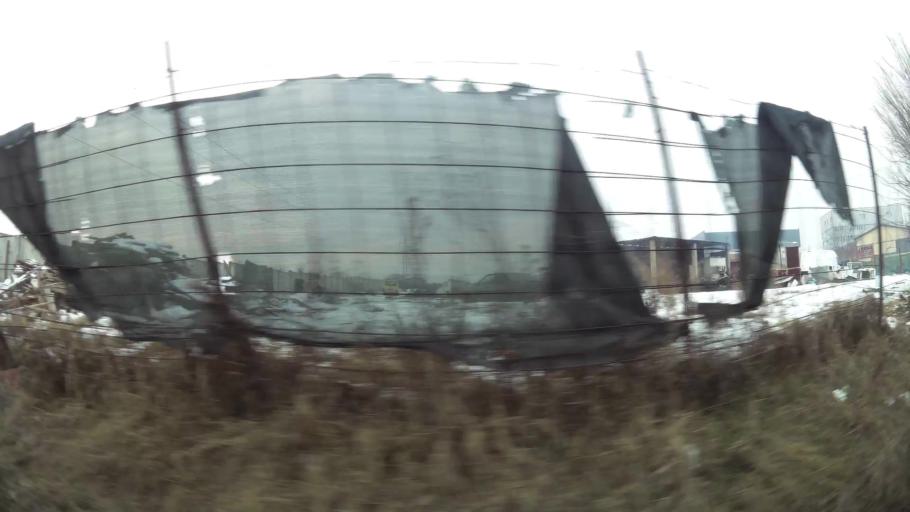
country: MK
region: Suto Orizari
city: Suto Orizare
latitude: 42.0467
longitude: 21.4279
